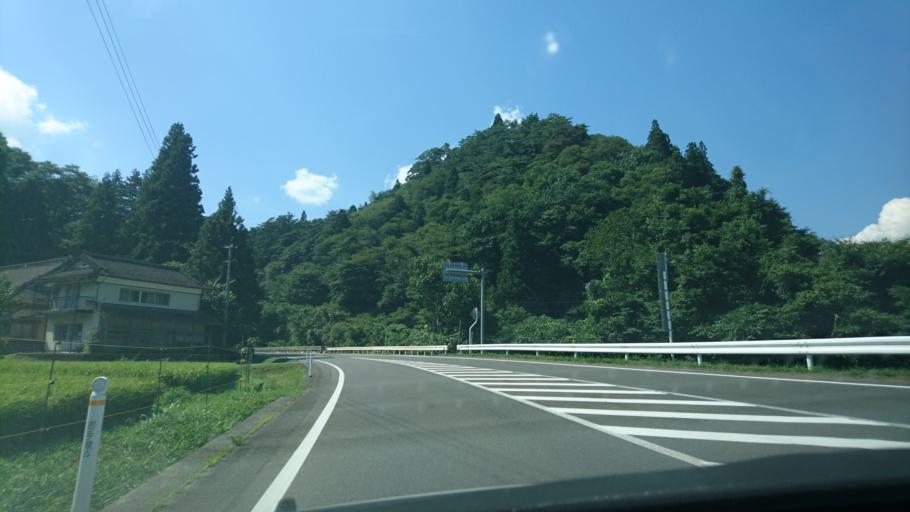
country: JP
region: Iwate
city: Ofunato
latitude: 39.0304
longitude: 141.5299
